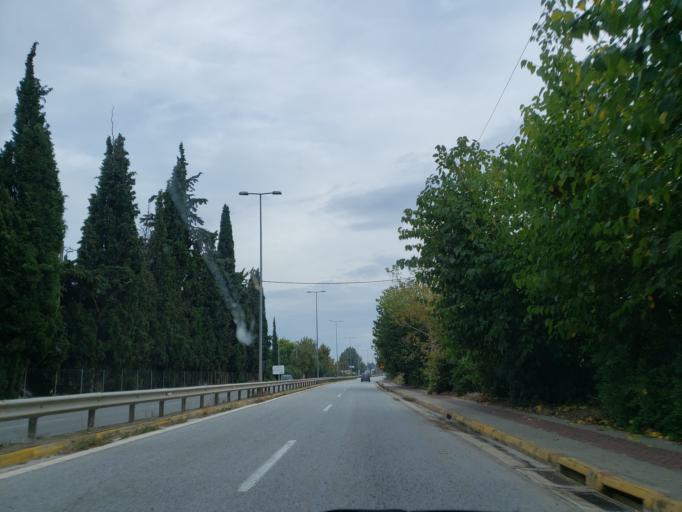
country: GR
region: Attica
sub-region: Nomarchia Anatolikis Attikis
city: Vrana
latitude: 38.1350
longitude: 23.9673
